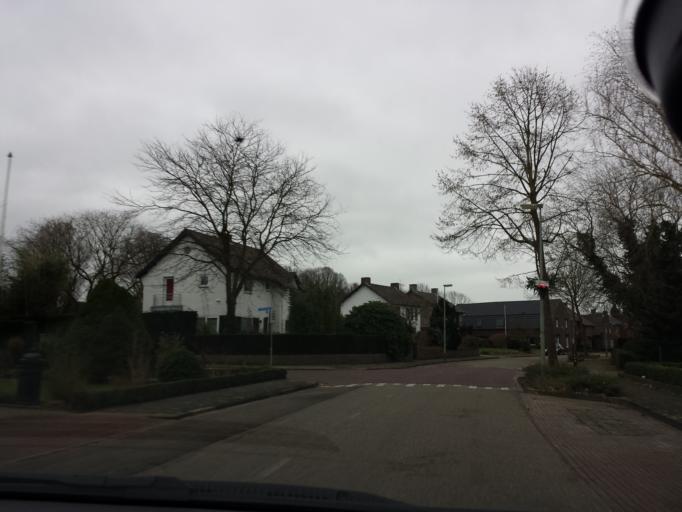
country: NL
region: Limburg
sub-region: Gemeente Roerdalen
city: Posterholt
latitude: 51.1255
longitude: 6.0283
